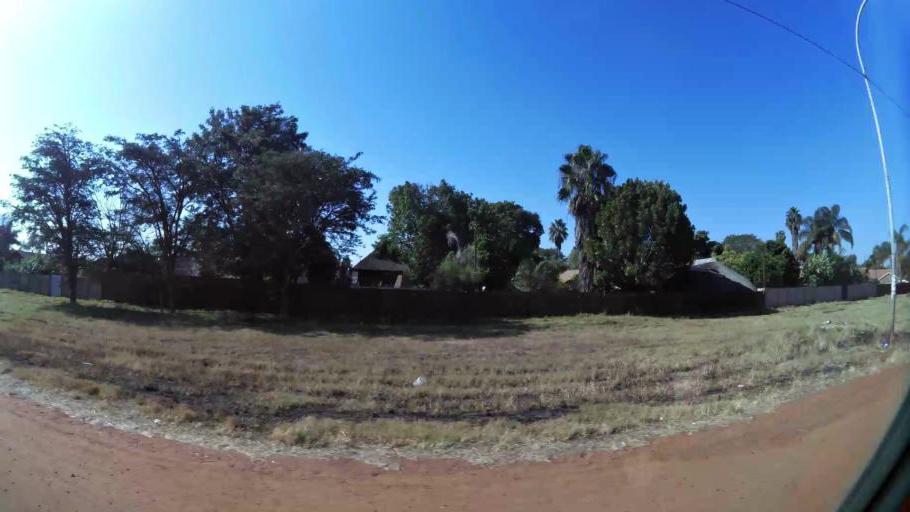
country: ZA
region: North-West
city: Ga-Rankuwa
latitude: -25.6463
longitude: 28.1027
